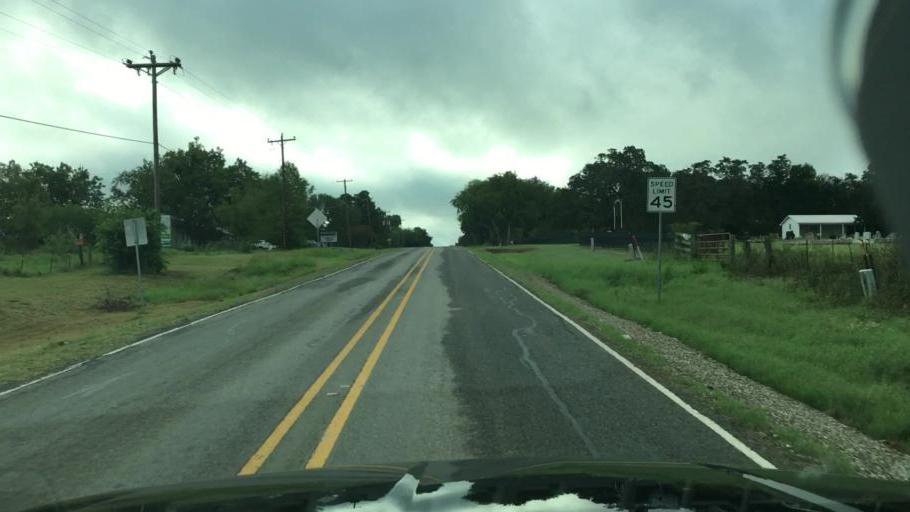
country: US
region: Texas
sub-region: Lee County
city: Lexington
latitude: 30.3645
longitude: -96.8342
